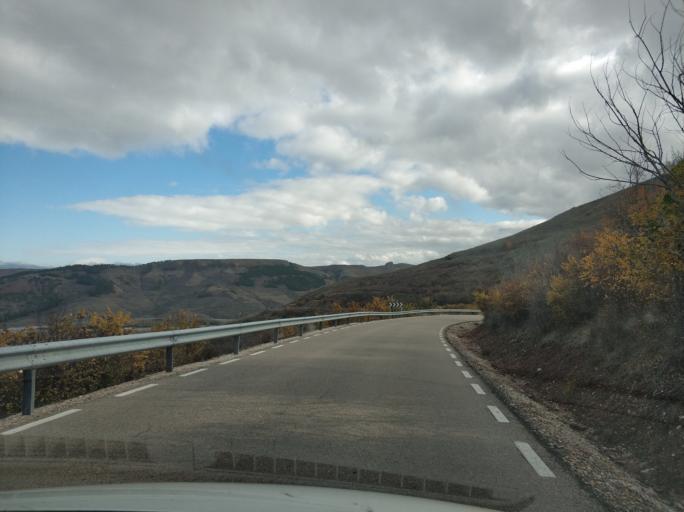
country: ES
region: Castille and Leon
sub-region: Provincia de Soria
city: Medinaceli
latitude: 41.1638
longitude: -2.4312
